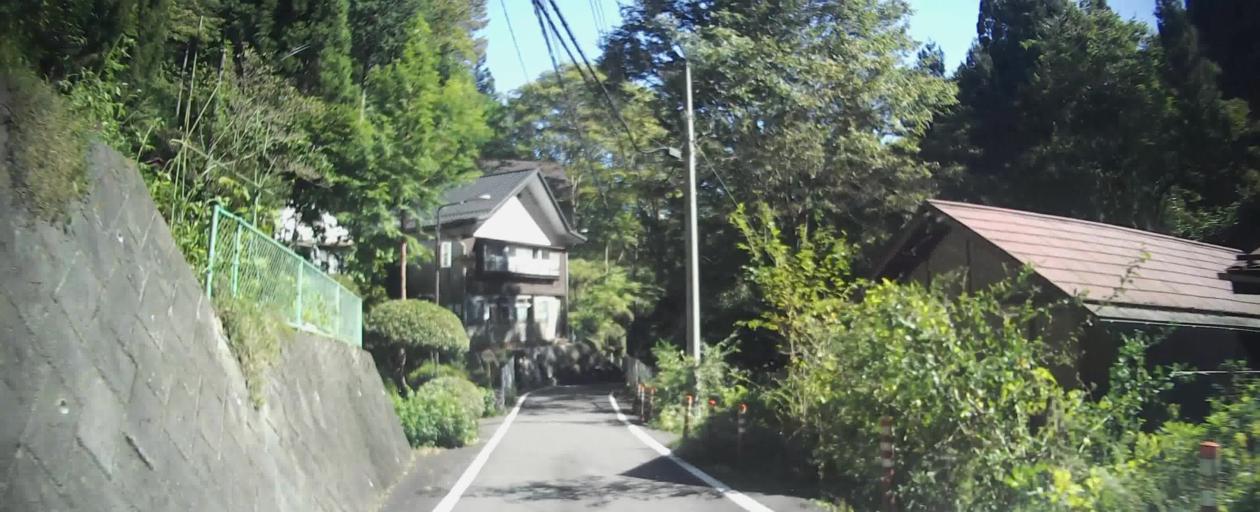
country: JP
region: Gunma
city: Nakanojomachi
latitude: 36.5752
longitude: 138.7331
